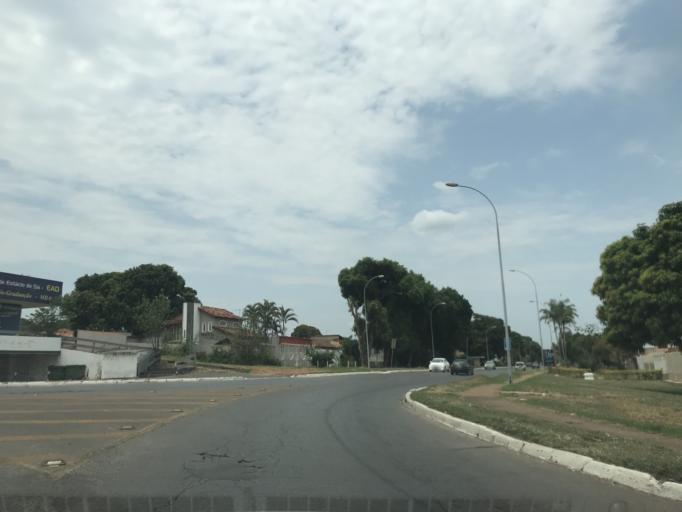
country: BR
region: Federal District
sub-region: Brasilia
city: Brasilia
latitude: -15.6520
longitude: -47.8043
